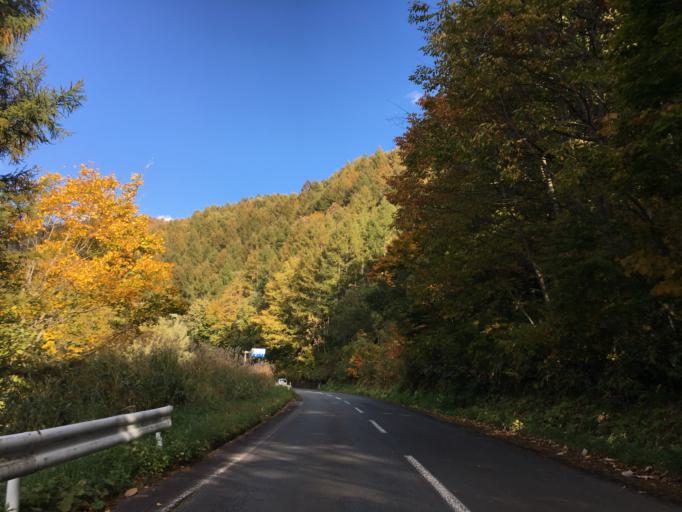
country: JP
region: Fukushima
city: Inawashiro
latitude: 37.6640
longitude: 140.1441
